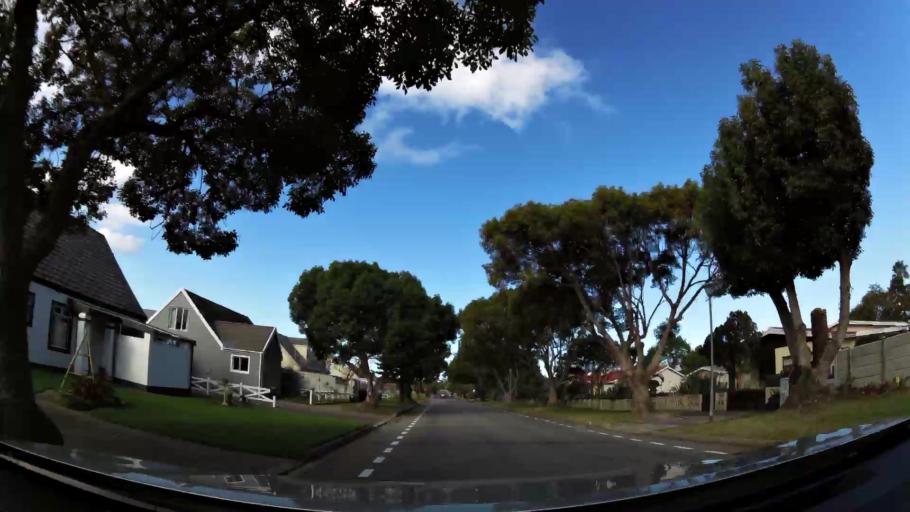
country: ZA
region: Western Cape
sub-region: Eden District Municipality
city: George
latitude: -33.9622
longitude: 22.4869
